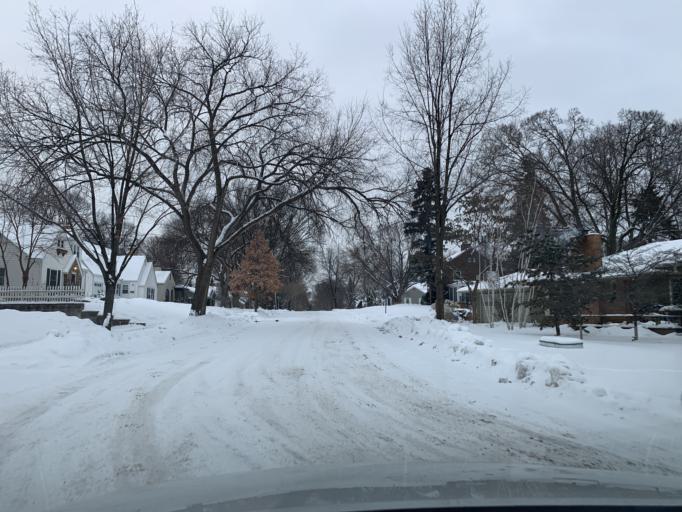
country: US
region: Minnesota
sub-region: Hennepin County
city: Saint Louis Park
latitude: 44.9333
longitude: -93.3367
